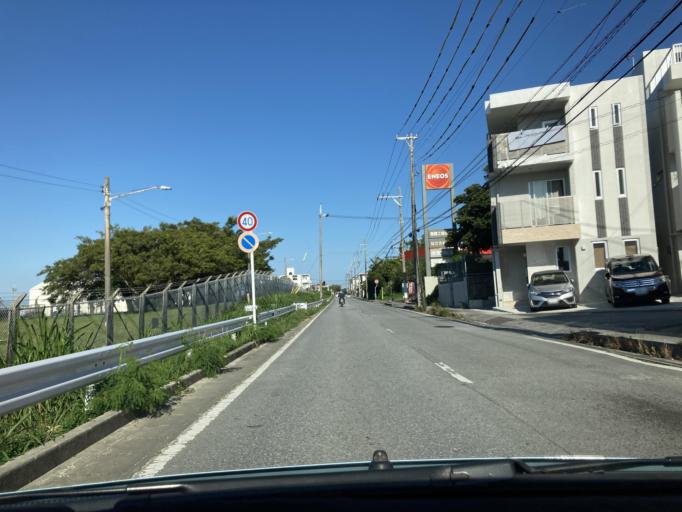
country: JP
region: Okinawa
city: Ginowan
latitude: 26.2648
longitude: 127.7546
